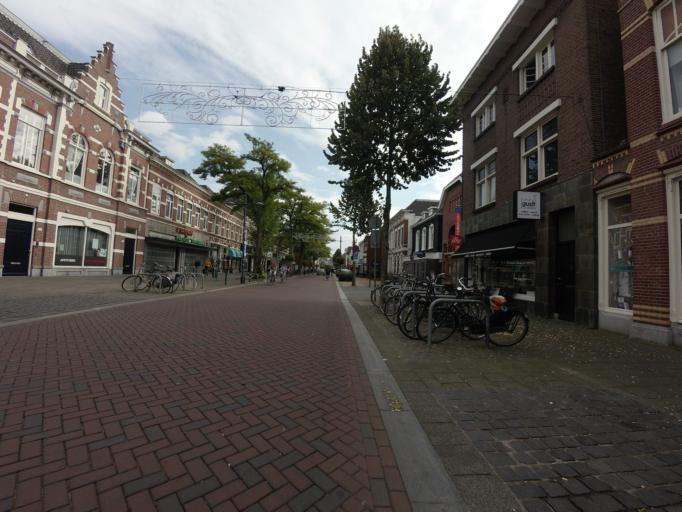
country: NL
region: North Brabant
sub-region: Gemeente Breda
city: Breda
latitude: 51.5781
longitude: 4.7797
